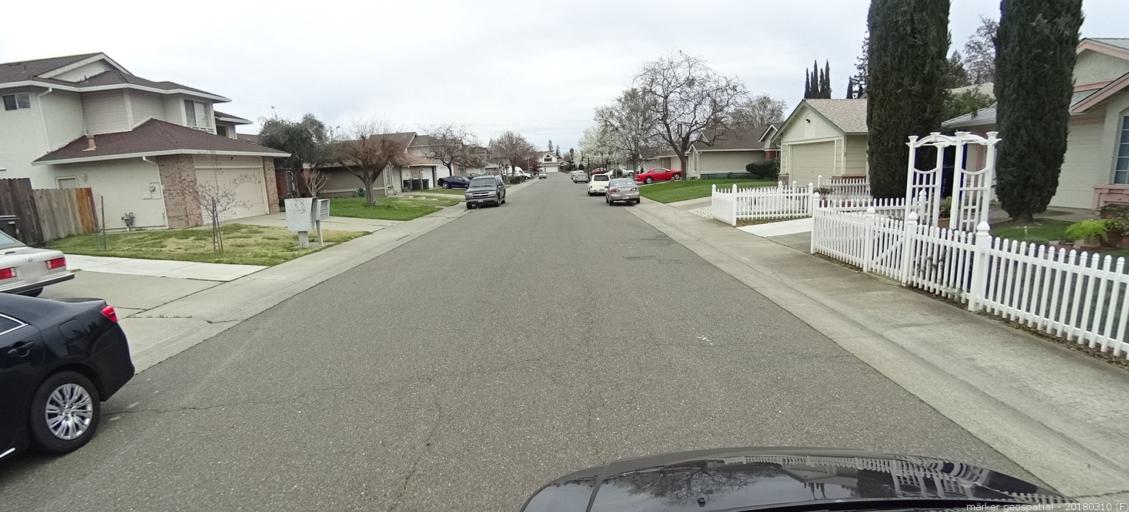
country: US
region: California
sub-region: Sacramento County
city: Vineyard
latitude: 38.4580
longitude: -121.3772
